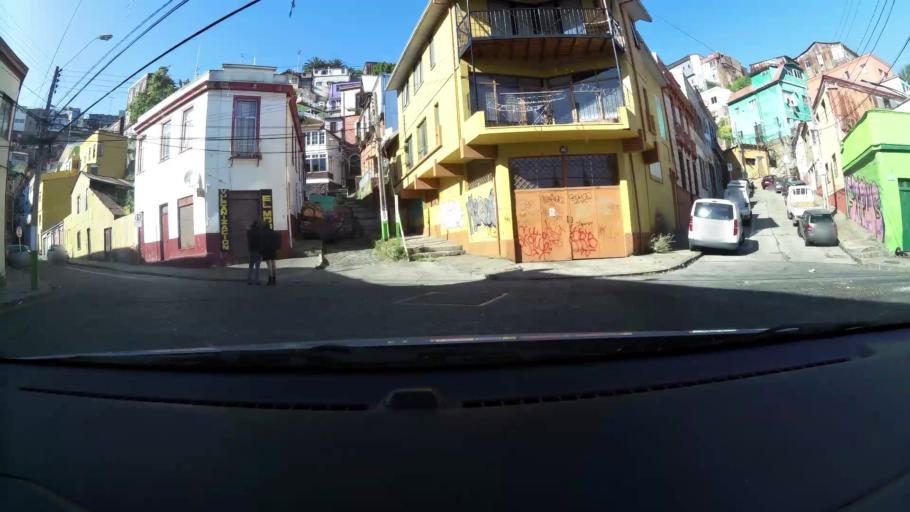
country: CL
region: Valparaiso
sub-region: Provincia de Valparaiso
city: Valparaiso
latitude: -33.0498
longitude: -71.6166
